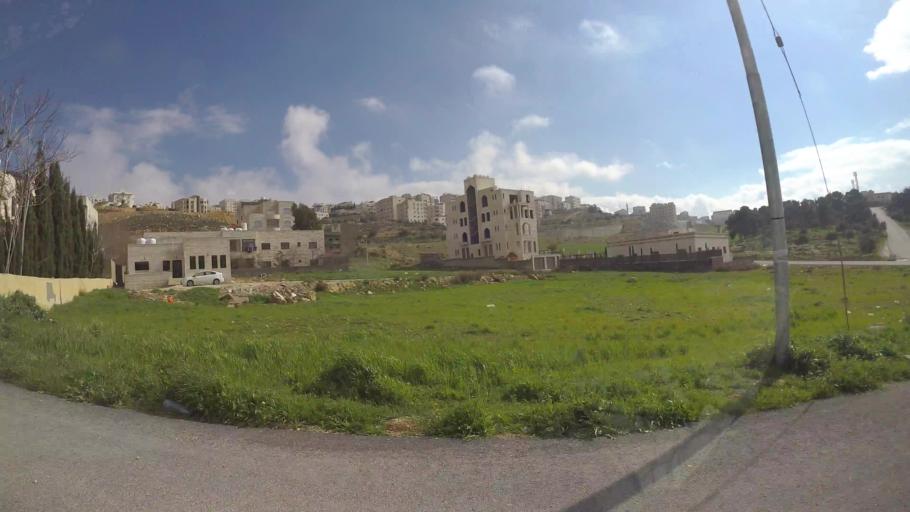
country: JO
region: Amman
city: Al Jubayhah
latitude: 32.0696
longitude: 35.8716
